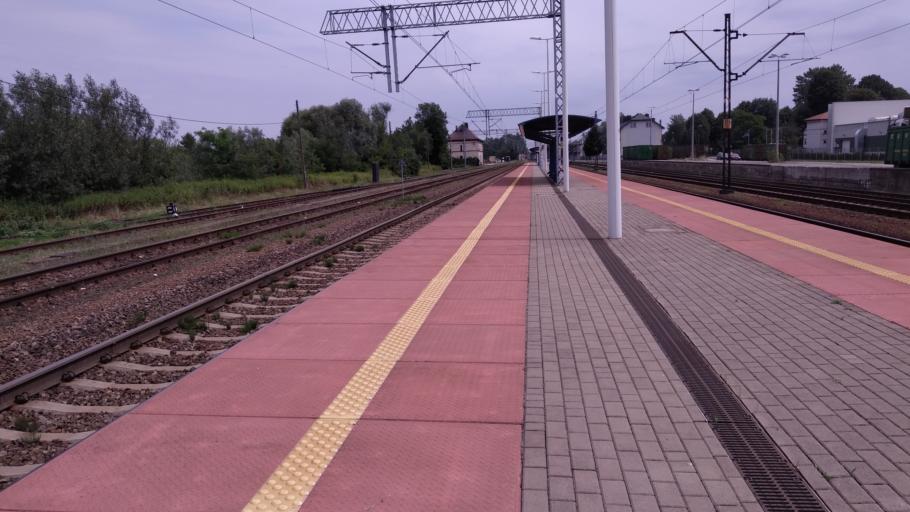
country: PL
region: Subcarpathian Voivodeship
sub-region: Powiat lancucki
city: Lancut
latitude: 50.0818
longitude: 22.2243
